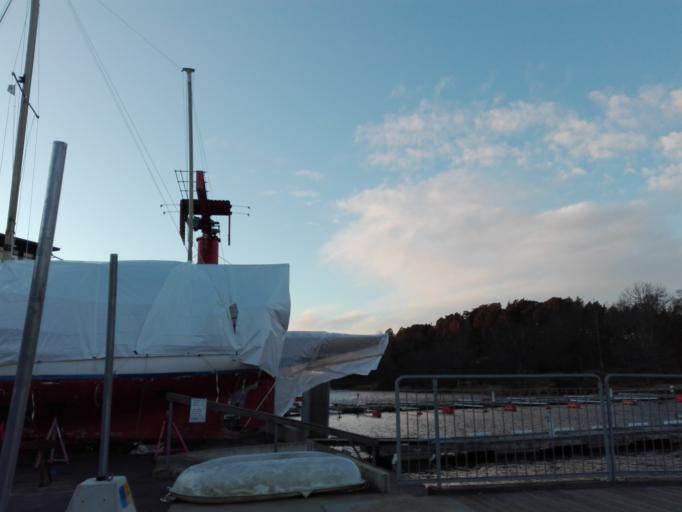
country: SE
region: Stockholm
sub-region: Nacka Kommun
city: Fisksatra
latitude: 59.2959
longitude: 18.2604
